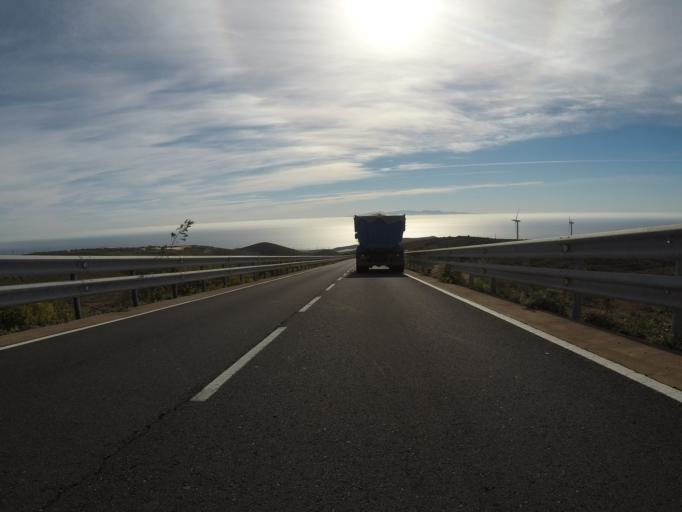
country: ES
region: Canary Islands
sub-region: Provincia de Santa Cruz de Tenerife
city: Lomo de Arico
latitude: 28.1612
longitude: -16.4878
